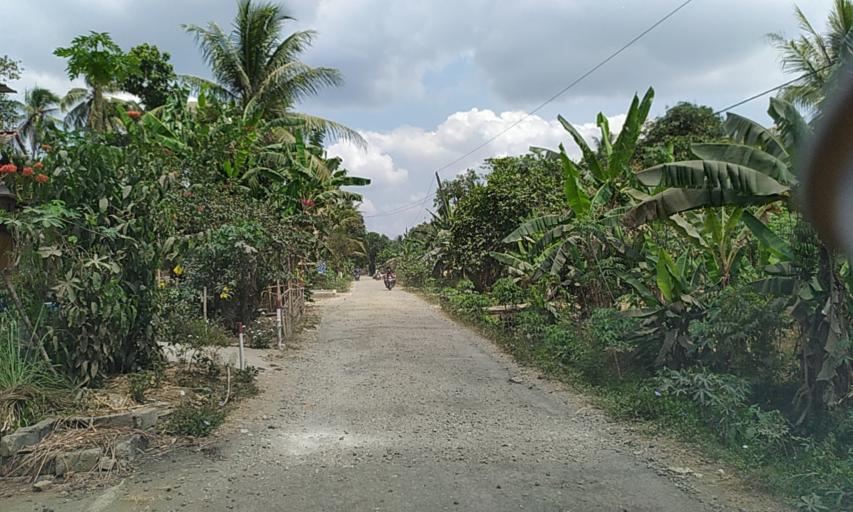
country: ID
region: Central Java
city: Purwosari
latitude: -7.3889
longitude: 108.7907
